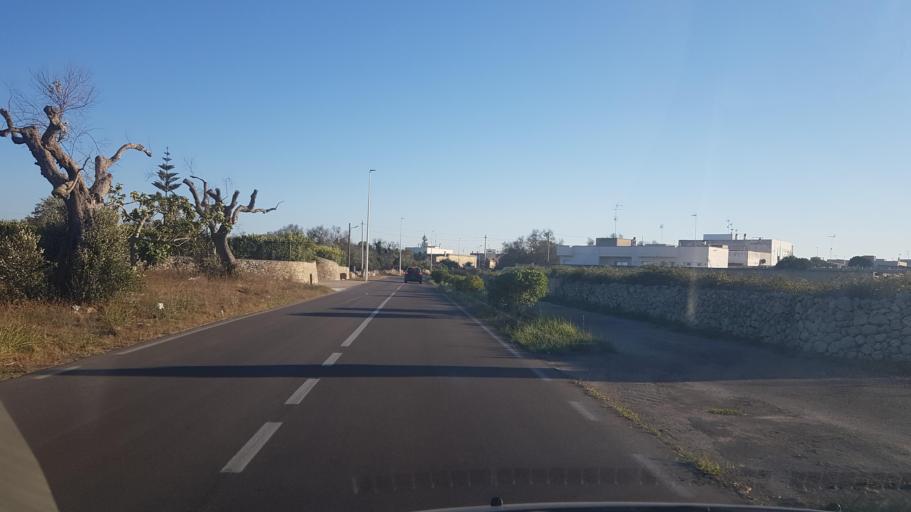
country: IT
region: Apulia
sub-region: Provincia di Lecce
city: Struda
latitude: 40.3241
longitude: 18.2859
